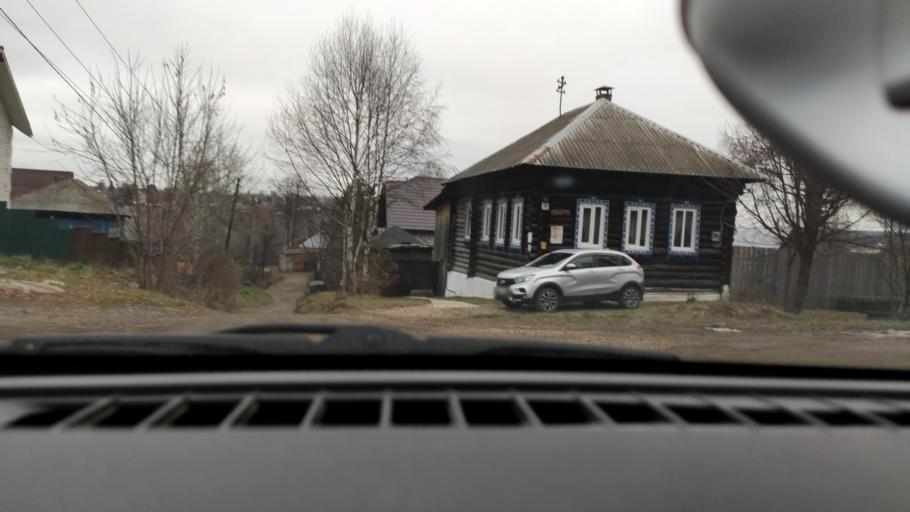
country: RU
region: Perm
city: Perm
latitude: 58.0296
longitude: 56.3339
